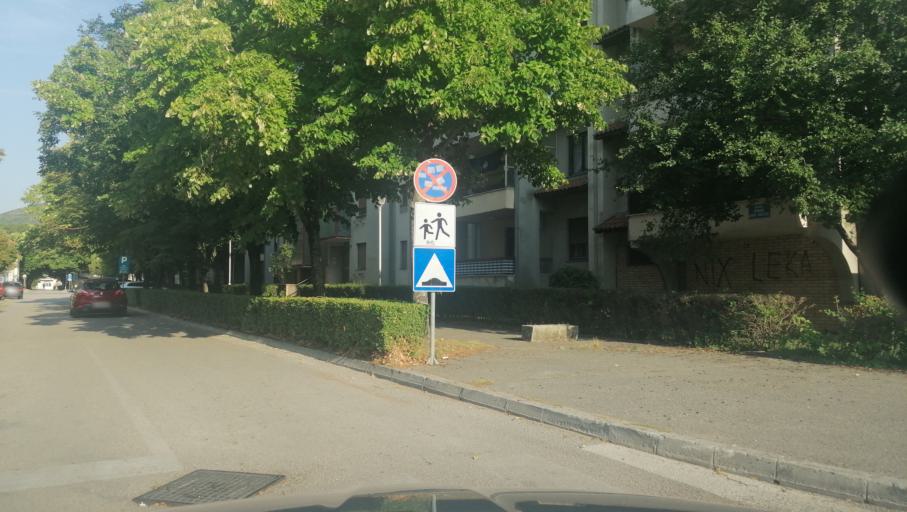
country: BA
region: Republika Srpska
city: Trebinje
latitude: 42.7070
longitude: 18.3440
